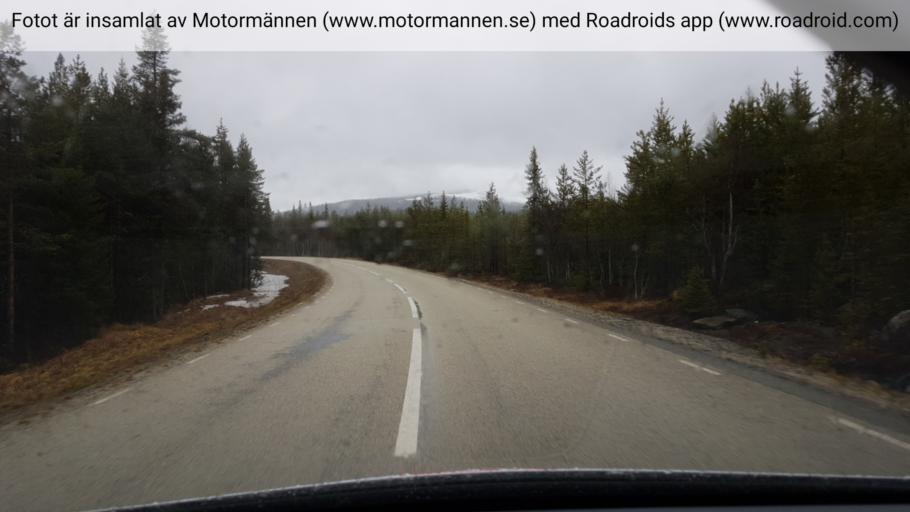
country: SE
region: Jaemtland
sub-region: Are Kommun
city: Are
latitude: 62.8215
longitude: 12.9234
